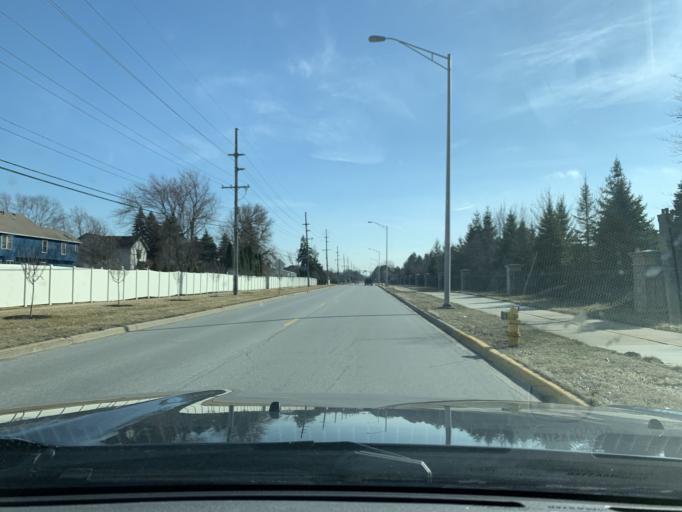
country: US
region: Indiana
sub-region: Lake County
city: Munster
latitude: 41.5336
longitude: -87.4904
